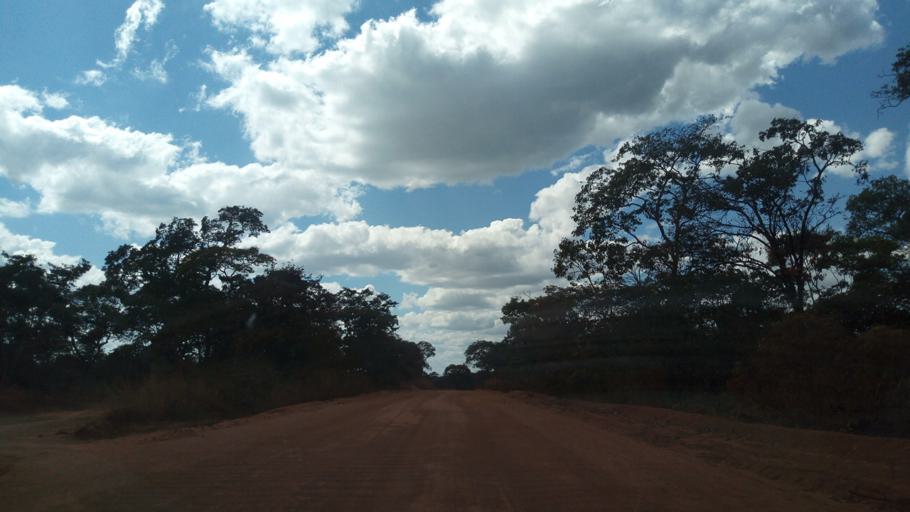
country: ZM
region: Copperbelt
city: Mufulira
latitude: -12.0336
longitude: 28.6712
